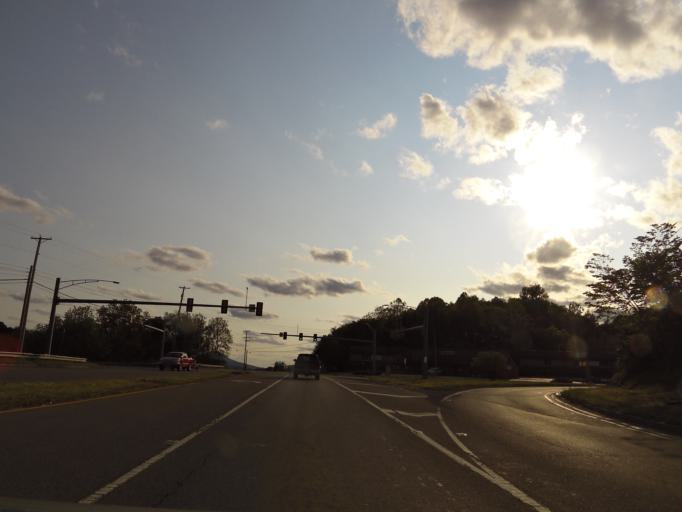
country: US
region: Virginia
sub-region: Tazewell County
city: Claypool Hill
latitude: 37.0629
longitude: -81.7513
